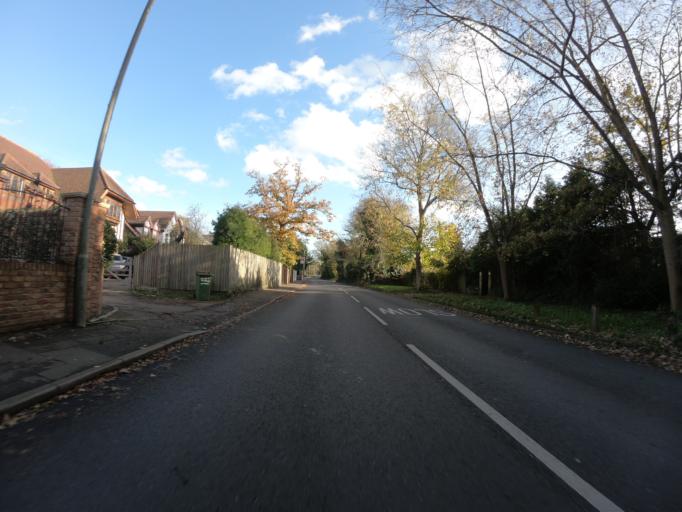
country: GB
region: England
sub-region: Greater London
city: Chislehurst
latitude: 51.4010
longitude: 0.0884
